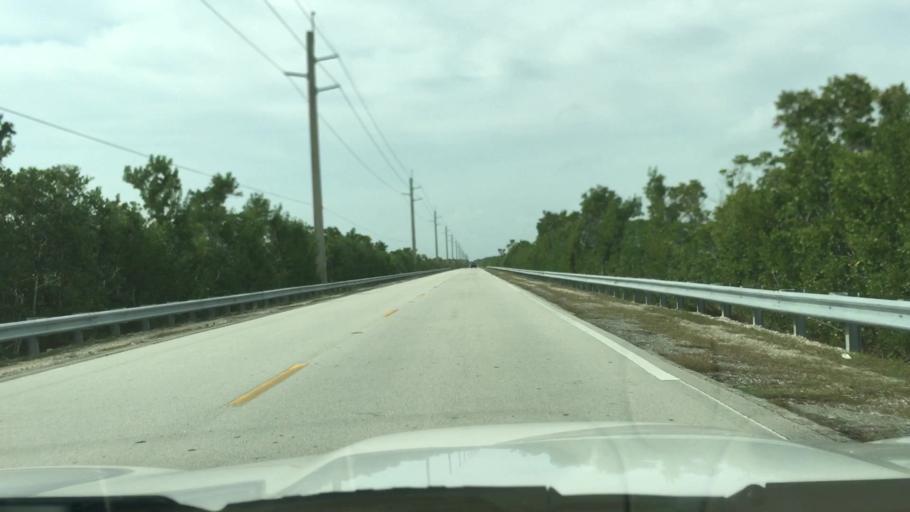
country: US
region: Florida
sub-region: Monroe County
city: North Key Largo
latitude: 25.2841
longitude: -80.3144
